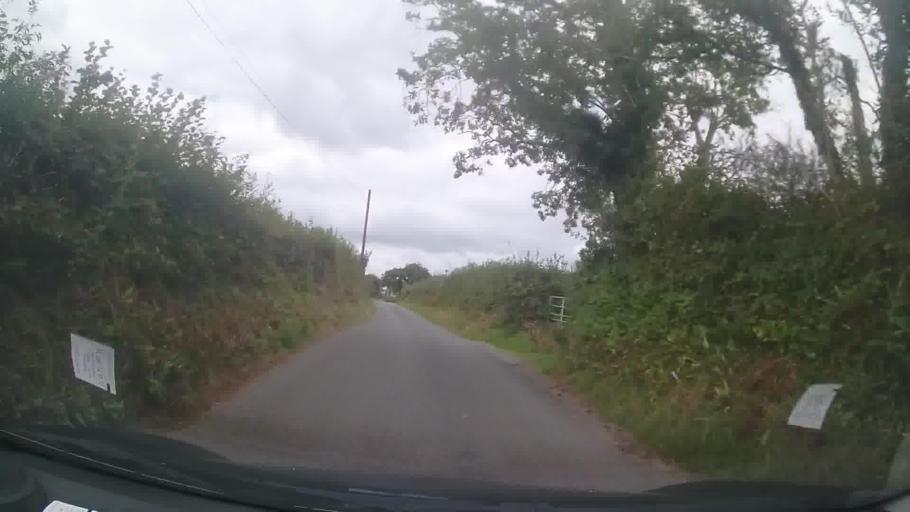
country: GB
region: Wales
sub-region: Pembrokeshire
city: Saundersfoot
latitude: 51.7429
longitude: -4.6596
